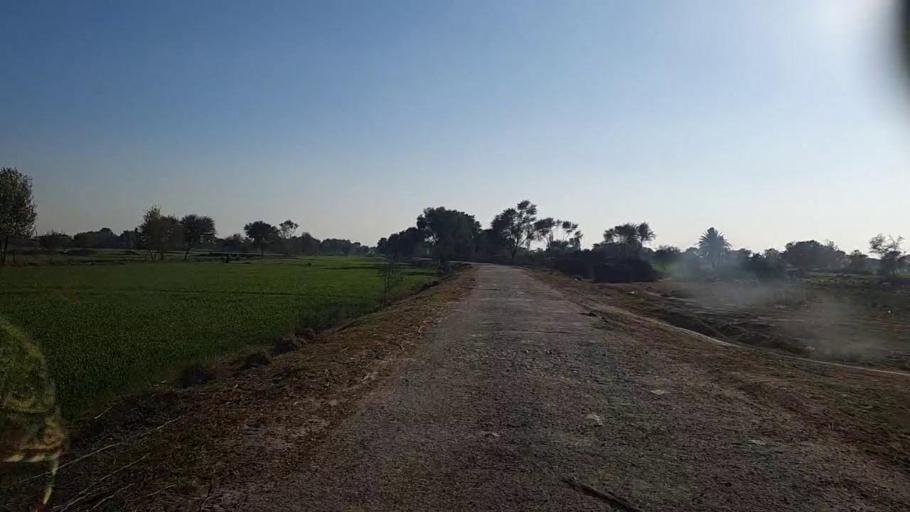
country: PK
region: Sindh
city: Khairpur
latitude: 28.0052
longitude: 69.7200
